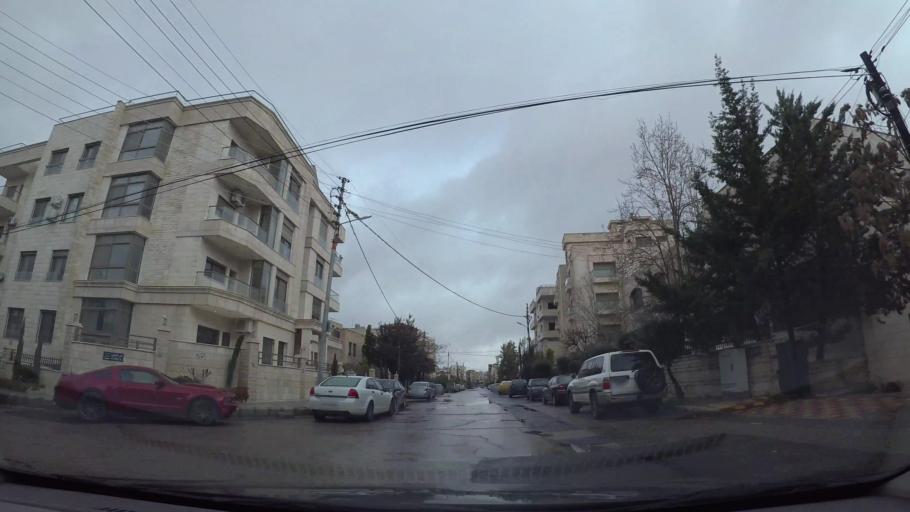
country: JO
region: Amman
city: Wadi as Sir
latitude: 31.9653
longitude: 35.8620
